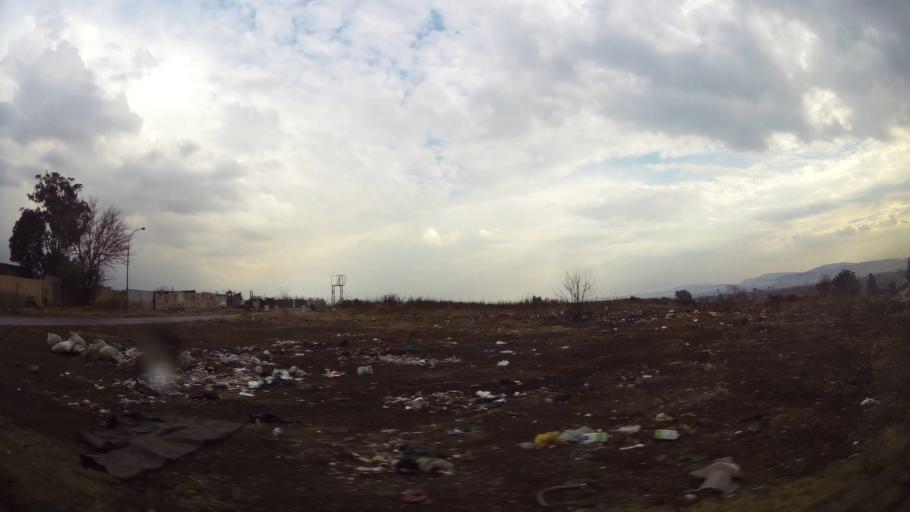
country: ZA
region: Gauteng
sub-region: Ekurhuleni Metropolitan Municipality
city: Germiston
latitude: -26.3757
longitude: 28.1241
